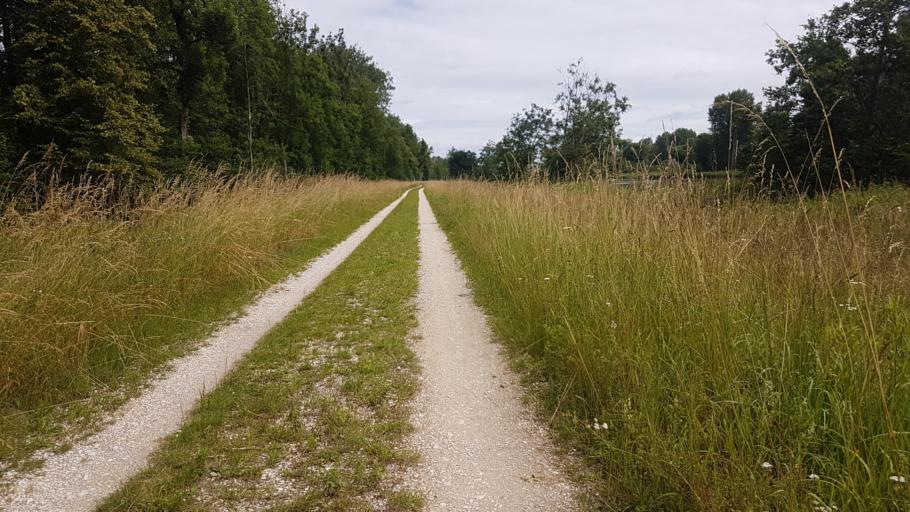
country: DE
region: Bavaria
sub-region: Swabia
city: Gundelfingen
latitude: 48.5289
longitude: 10.3885
